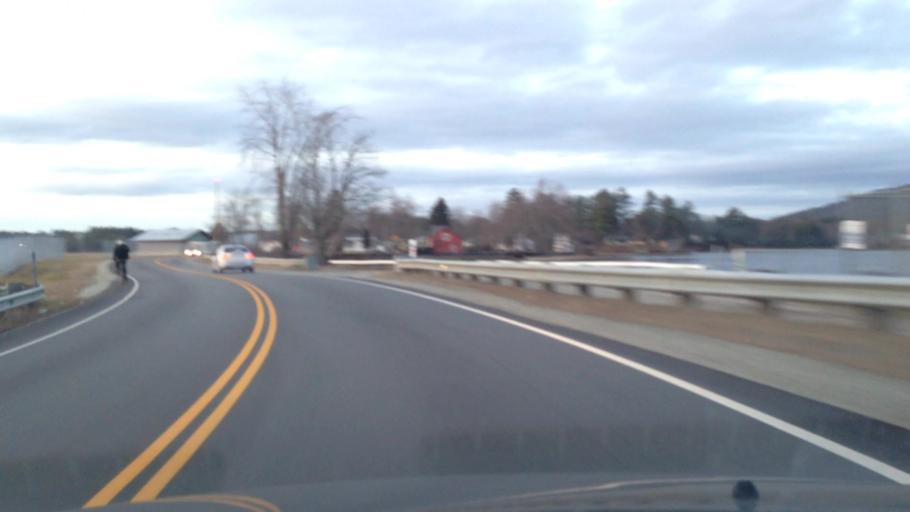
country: US
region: New Hampshire
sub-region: Cheshire County
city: Swanzey
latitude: 42.8979
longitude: -72.2634
